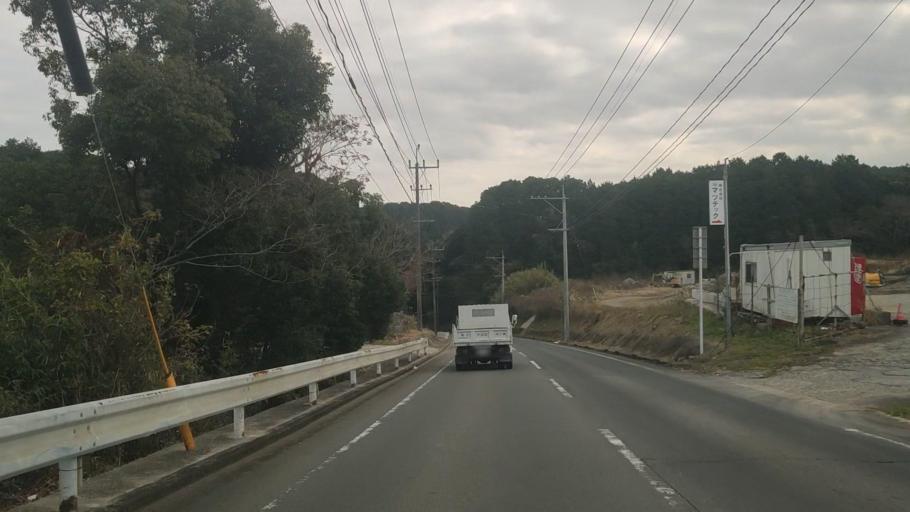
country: JP
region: Nagasaki
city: Shimabara
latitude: 32.8526
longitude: 130.2624
